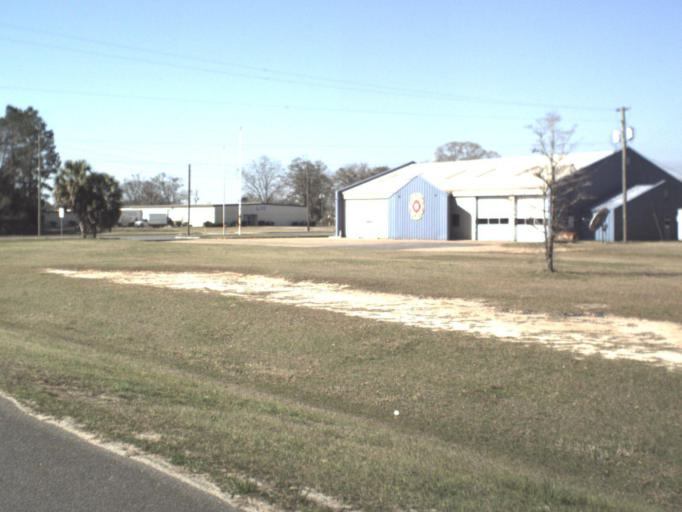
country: US
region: Florida
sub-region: Jackson County
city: Marianna
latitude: 30.8238
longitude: -85.1699
